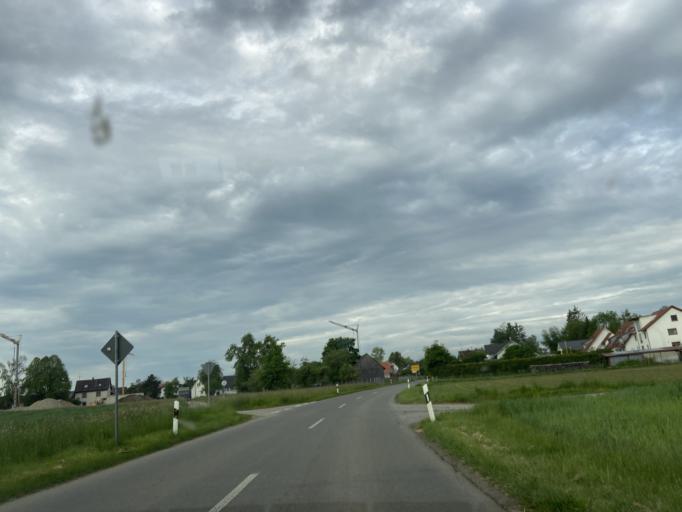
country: DE
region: Baden-Wuerttemberg
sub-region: Tuebingen Region
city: Hohentengen
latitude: 48.0380
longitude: 9.3733
